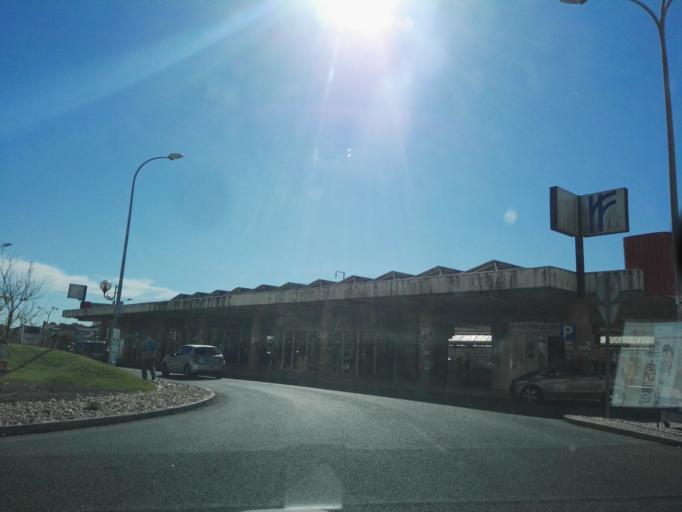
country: PT
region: Lisbon
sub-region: Sintra
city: Rio de Mouro
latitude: 38.7938
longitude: -9.3303
